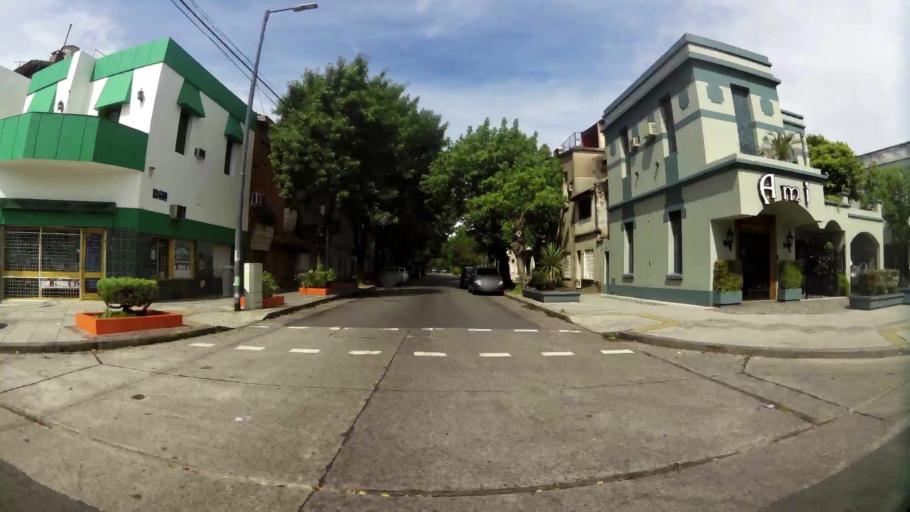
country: AR
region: Buenos Aires
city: San Justo
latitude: -34.6416
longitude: -58.5249
